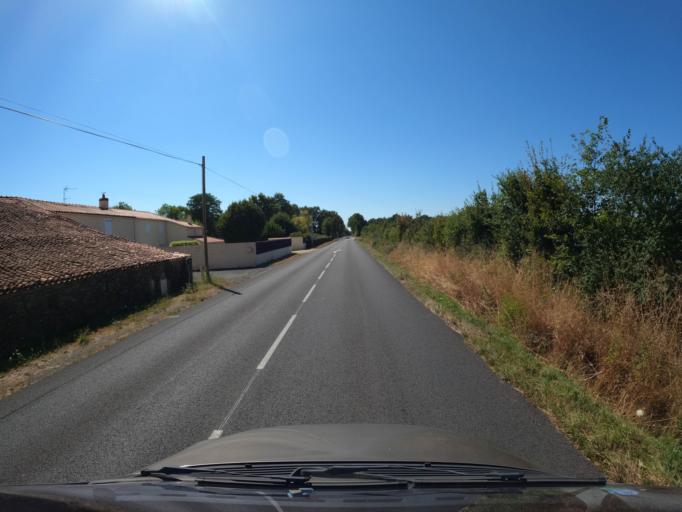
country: FR
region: Pays de la Loire
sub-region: Departement de la Vendee
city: Saint-Georges-de-Montaigu
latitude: 46.9647
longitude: -1.2761
